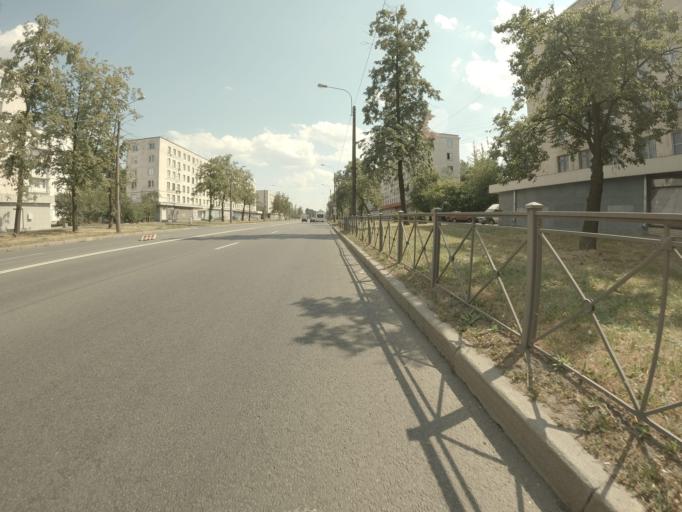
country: RU
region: St.-Petersburg
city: Avtovo
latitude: 59.8689
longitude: 30.2726
